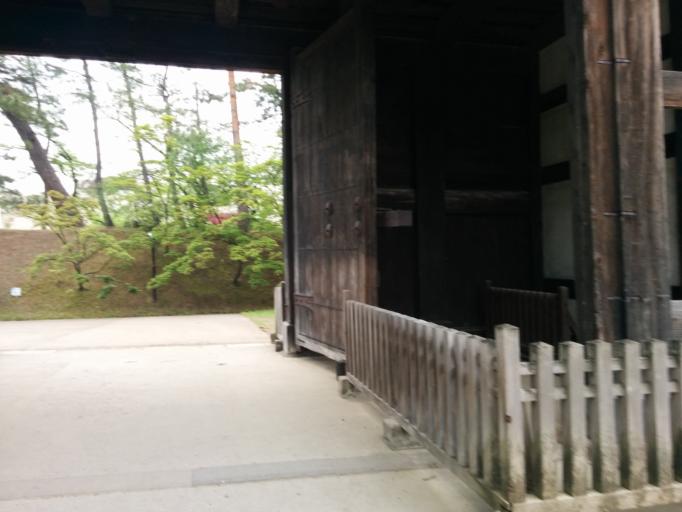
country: JP
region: Aomori
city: Hirosaki
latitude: 40.6072
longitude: 140.4676
